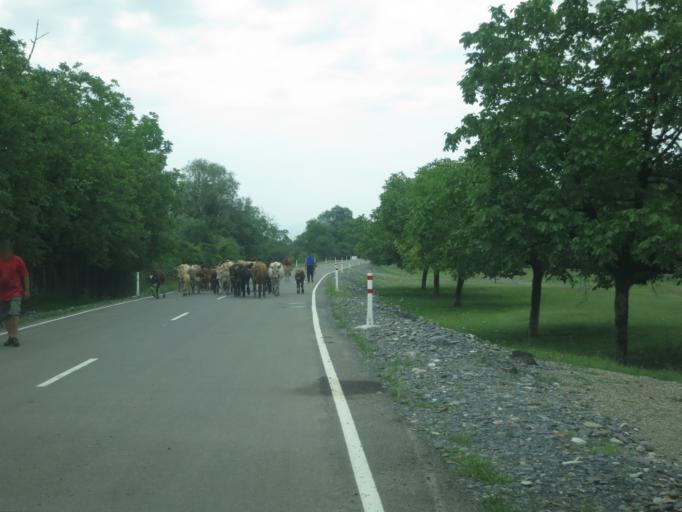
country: GE
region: Kakheti
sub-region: Telavi
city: Telavi
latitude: 42.1244
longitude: 45.4246
